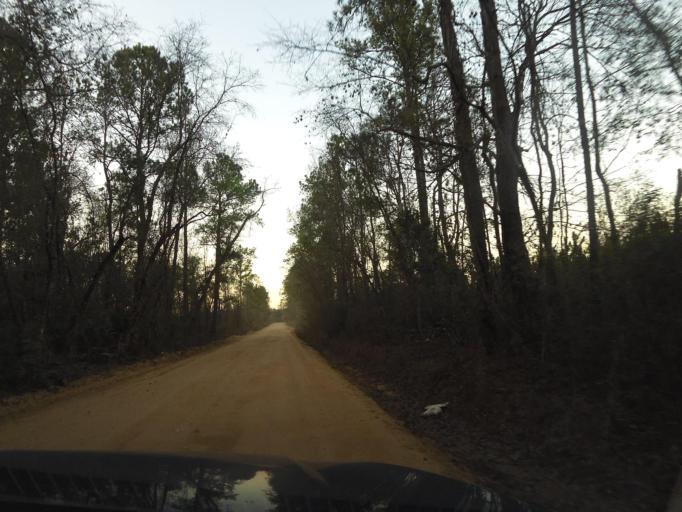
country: US
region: Florida
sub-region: Clay County
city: Asbury Lake
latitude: 29.9526
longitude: -81.7889
